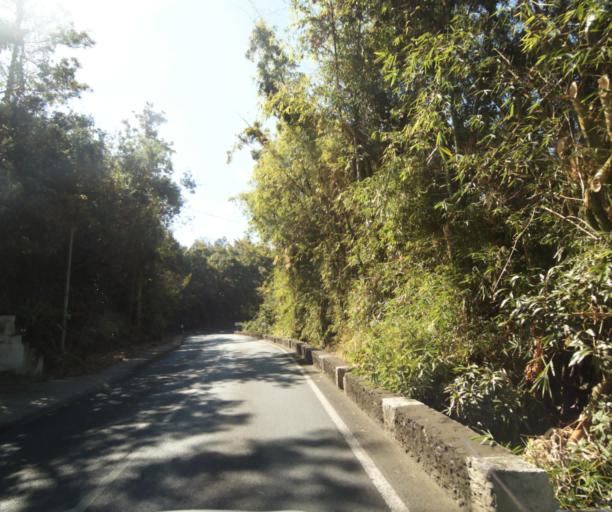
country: RE
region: Reunion
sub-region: Reunion
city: Saint-Paul
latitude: -20.9935
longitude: 55.3308
